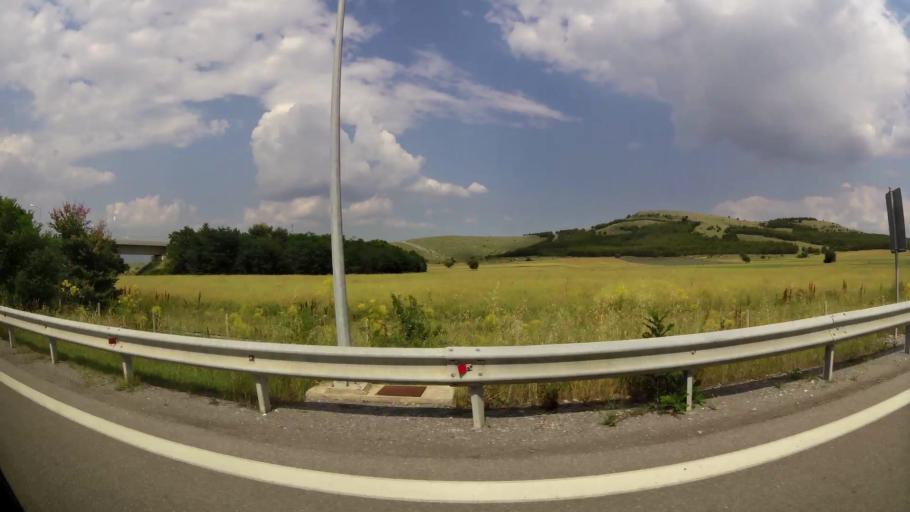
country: GR
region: West Macedonia
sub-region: Nomos Kozanis
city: Koila
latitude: 40.3494
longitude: 21.8079
